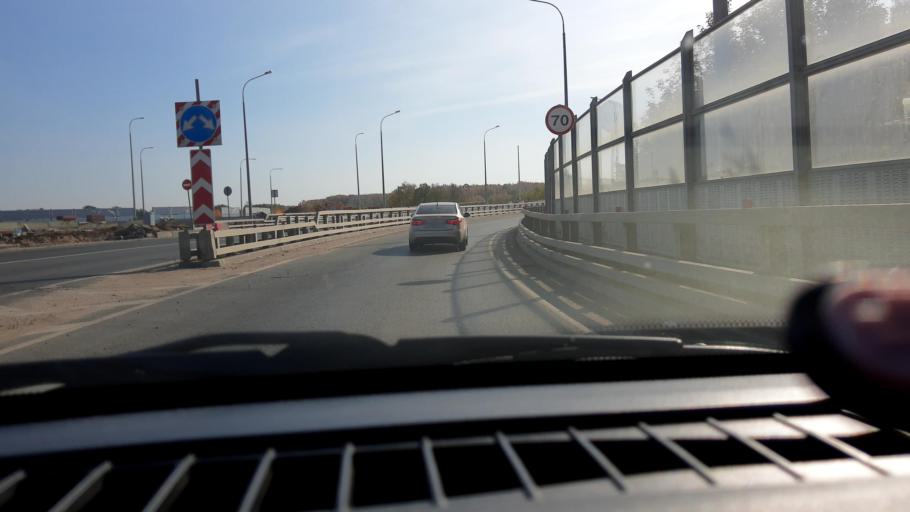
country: RU
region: Nizjnij Novgorod
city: Neklyudovo
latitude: 56.4003
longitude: 43.9892
